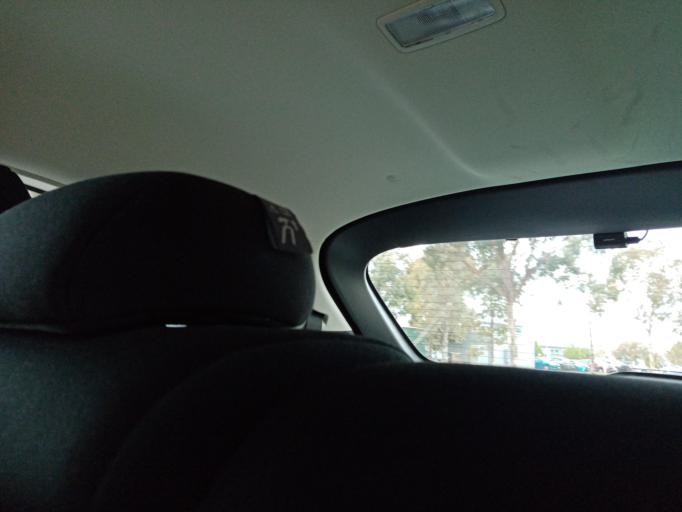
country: AU
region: Western Australia
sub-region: City of Cockburn
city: Success
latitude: -32.1327
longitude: 115.8551
